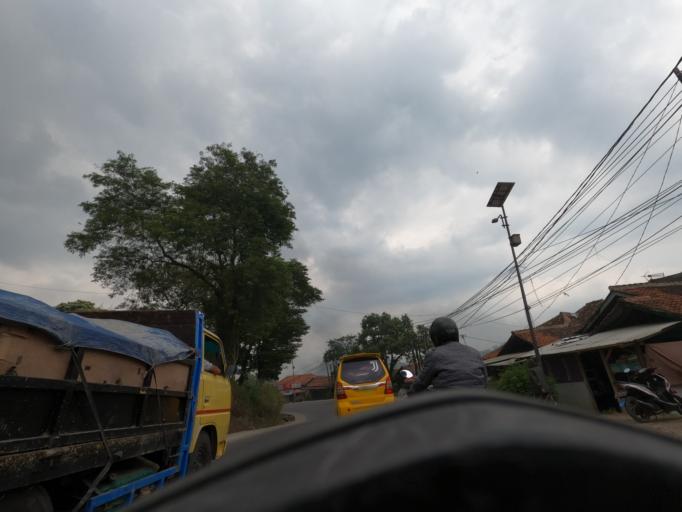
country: ID
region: West Java
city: Padalarang
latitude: -6.8310
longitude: 107.4421
